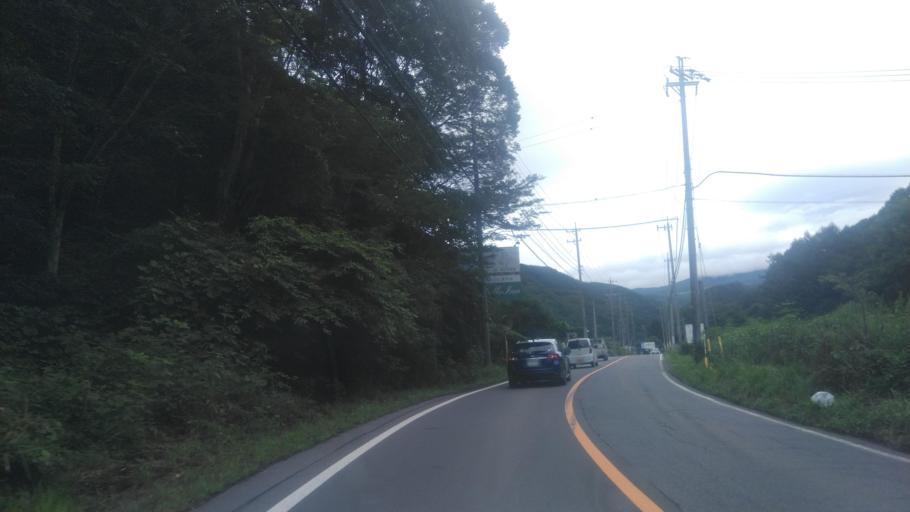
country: JP
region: Nagano
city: Ueda
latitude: 36.4702
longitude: 138.3430
